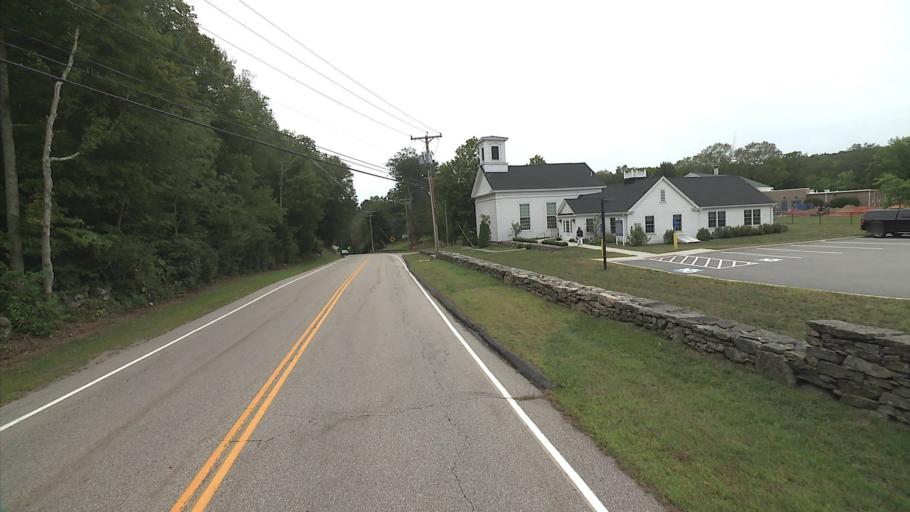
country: US
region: Connecticut
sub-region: Middlesex County
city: Essex Village
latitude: 41.4137
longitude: -72.3363
